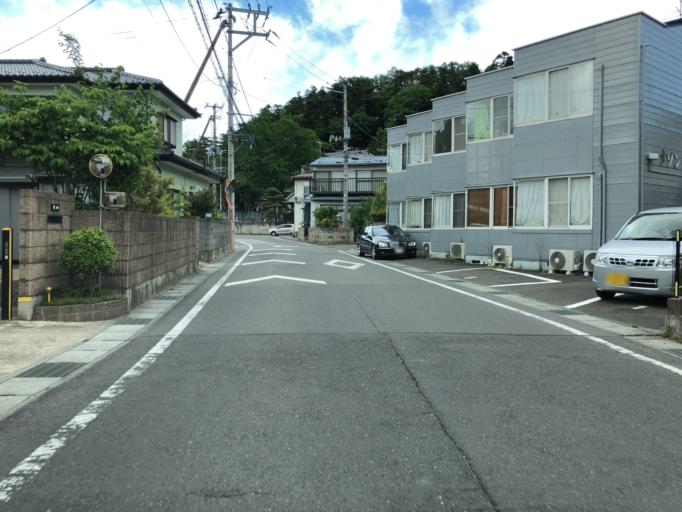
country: JP
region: Fukushima
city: Fukushima-shi
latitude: 37.7652
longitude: 140.4514
